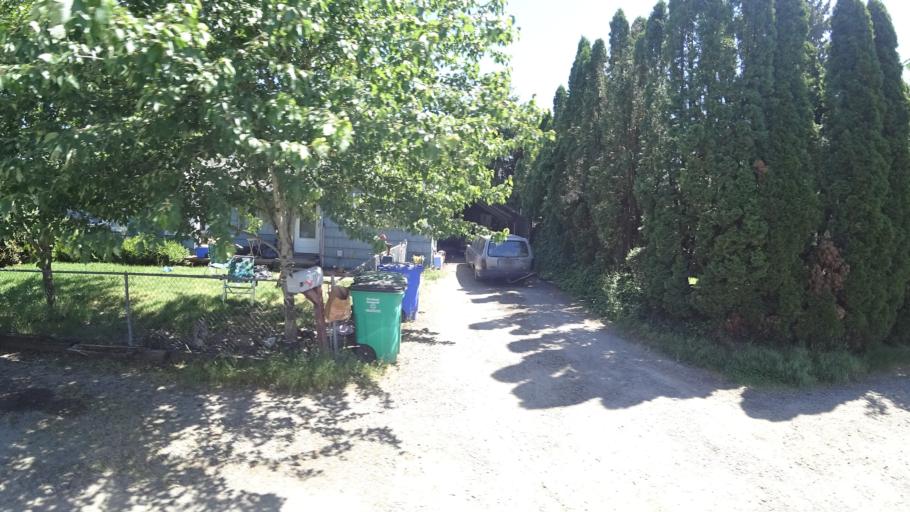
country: US
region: Oregon
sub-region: Clackamas County
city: Happy Valley
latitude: 45.4781
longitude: -122.5355
